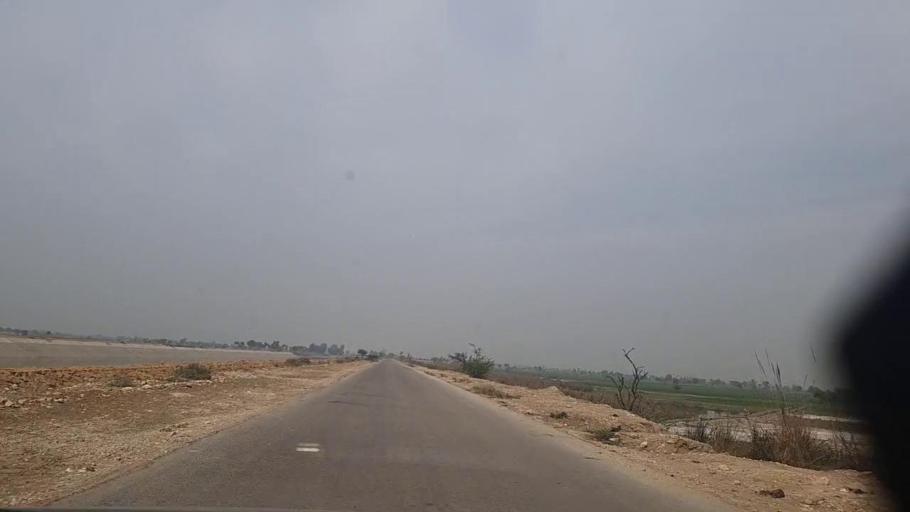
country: PK
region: Sindh
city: Sakrand
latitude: 26.2755
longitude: 68.2316
